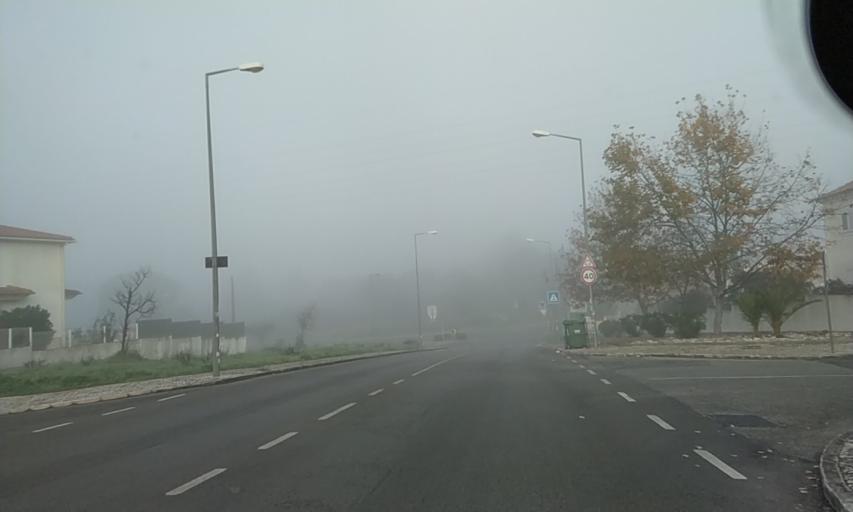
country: PT
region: Setubal
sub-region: Setubal
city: Setubal
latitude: 38.5447
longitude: -8.8548
